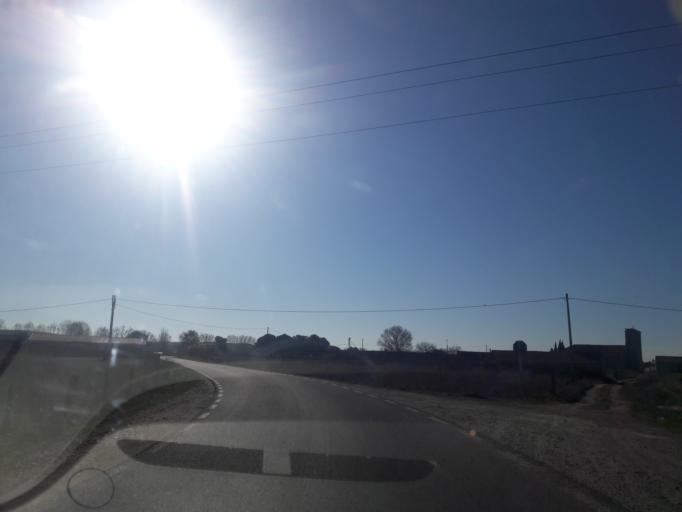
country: ES
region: Castille and Leon
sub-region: Provincia de Salamanca
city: Tordillos
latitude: 40.8569
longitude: -5.3557
